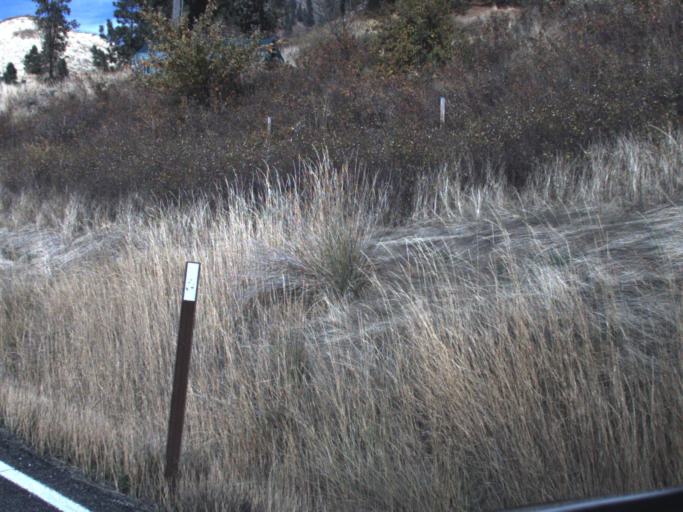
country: US
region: Washington
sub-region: Stevens County
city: Kettle Falls
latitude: 48.2827
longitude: -118.1371
